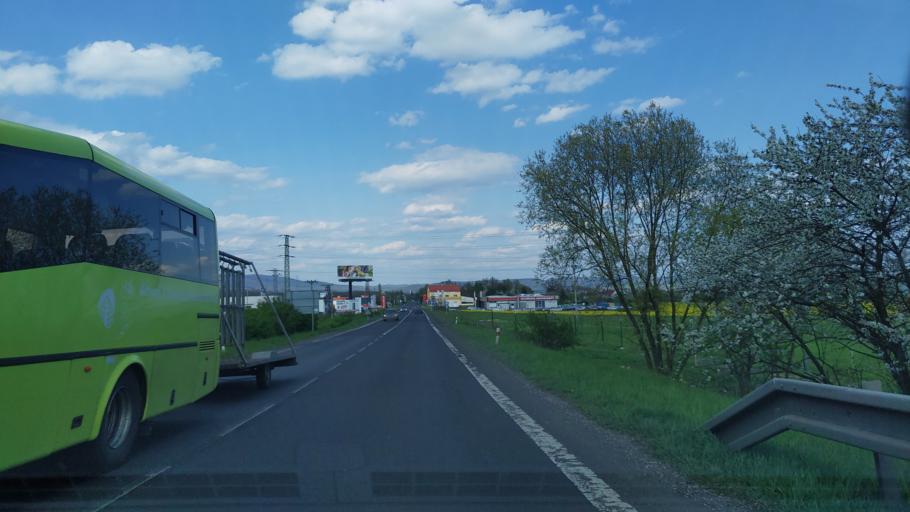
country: CZ
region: Ustecky
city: Probostov
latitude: 50.6567
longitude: 13.8600
